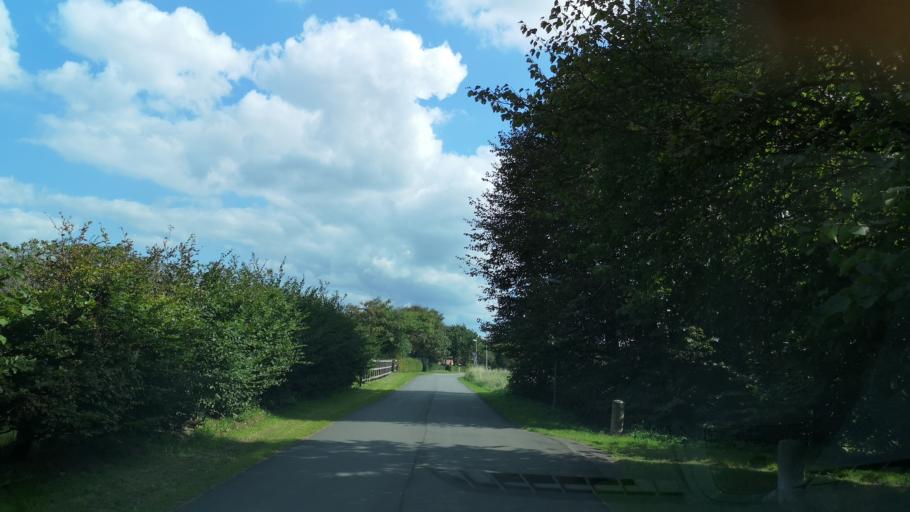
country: DK
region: Central Jutland
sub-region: Ringkobing-Skjern Kommune
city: Skjern
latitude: 55.8926
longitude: 8.4098
